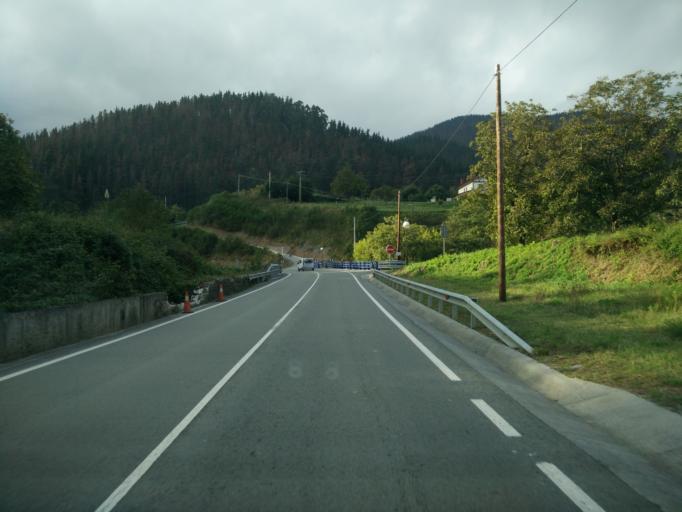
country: ES
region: Basque Country
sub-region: Bizkaia
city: Markina-Xemein
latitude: 43.2877
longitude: -2.4916
